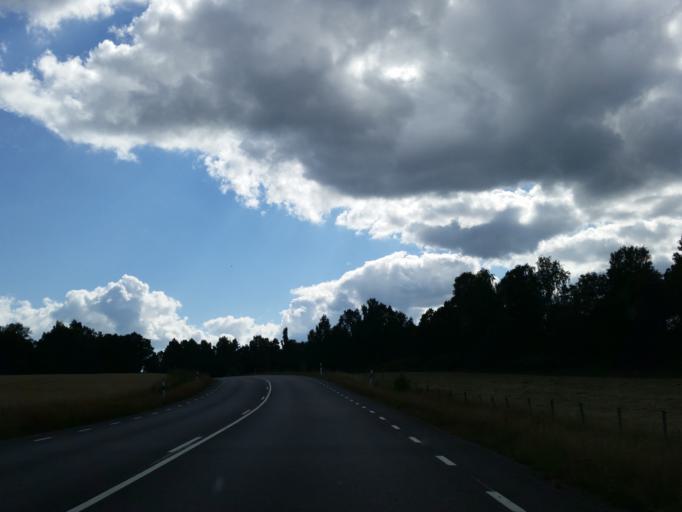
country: SE
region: Soedermanland
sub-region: Trosa Kommun
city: Vagnharad
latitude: 58.9631
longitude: 17.5627
